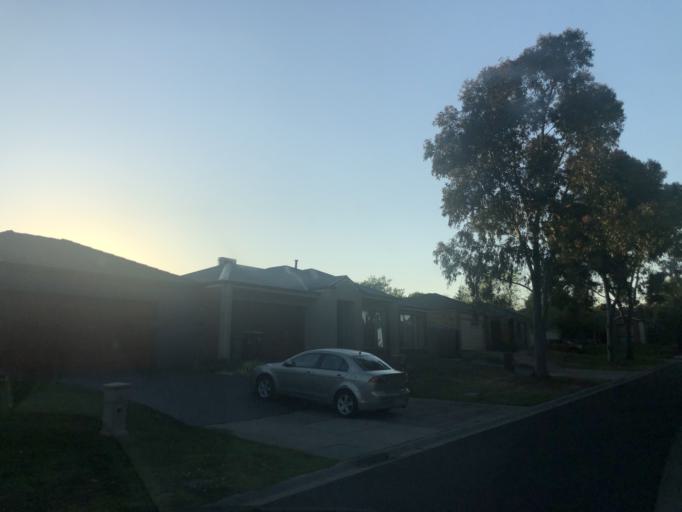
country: AU
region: Victoria
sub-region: Casey
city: Lynbrook
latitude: -38.0478
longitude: 145.2589
